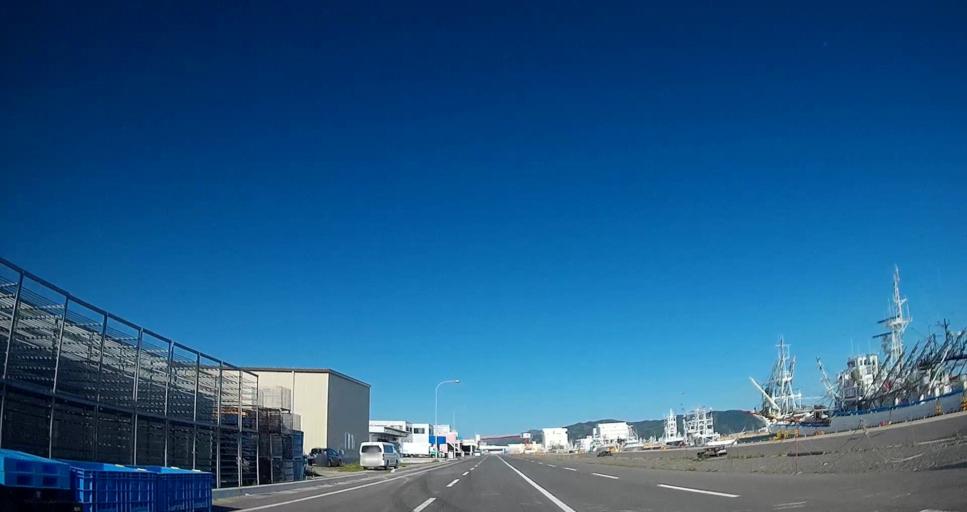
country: JP
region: Miyagi
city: Ishinomaki
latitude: 38.4119
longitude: 141.3191
